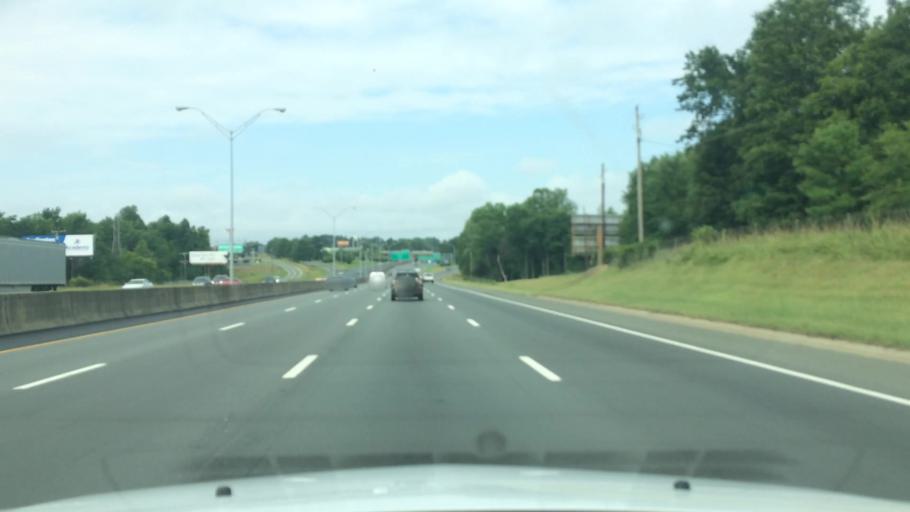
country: US
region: North Carolina
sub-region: Alamance County
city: Elon
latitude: 36.0686
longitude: -79.4910
